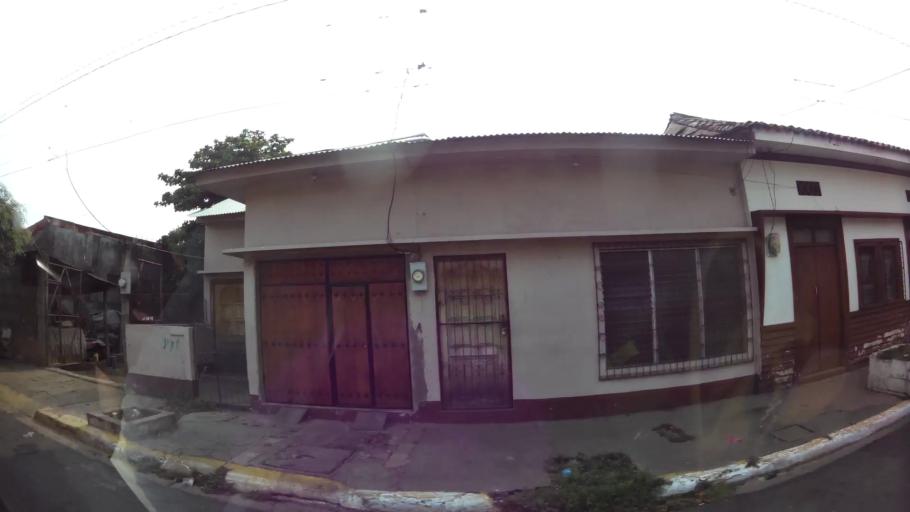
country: NI
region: Chinandega
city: Chinandega
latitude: 12.6252
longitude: -87.1336
